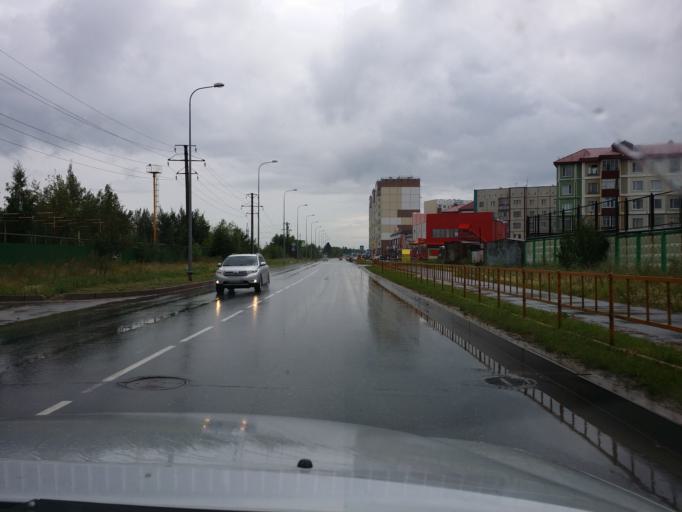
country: RU
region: Khanty-Mansiyskiy Avtonomnyy Okrug
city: Nizhnevartovsk
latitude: 60.9564
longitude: 76.5594
